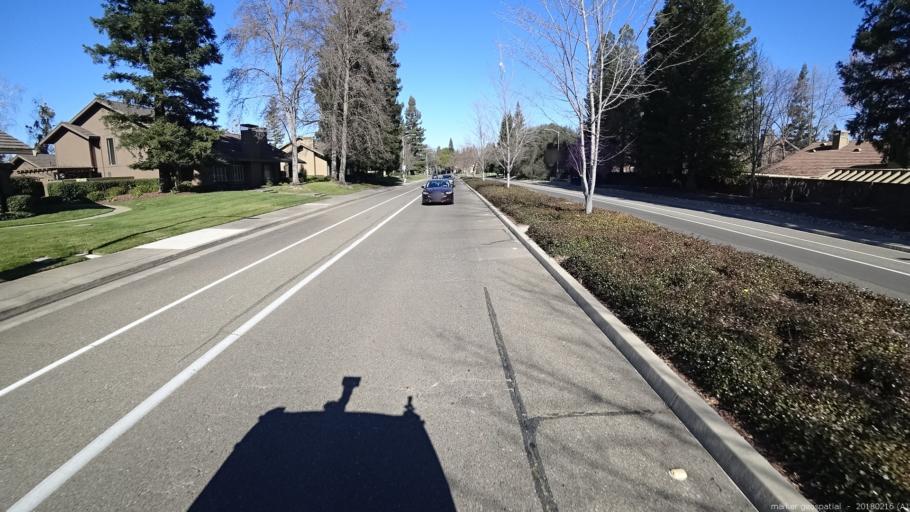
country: US
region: California
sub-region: Sacramento County
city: Gold River
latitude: 38.6288
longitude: -121.2518
